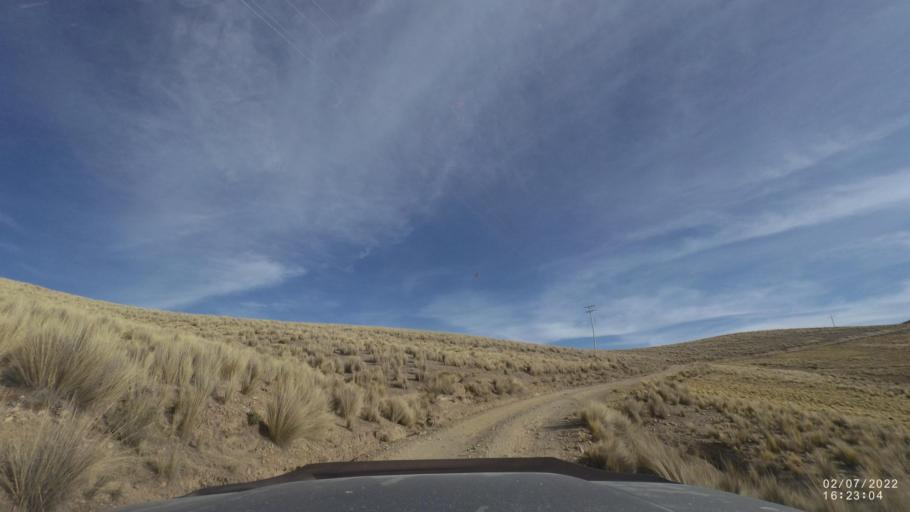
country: BO
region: Cochabamba
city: Irpa Irpa
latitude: -17.9380
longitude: -66.4570
